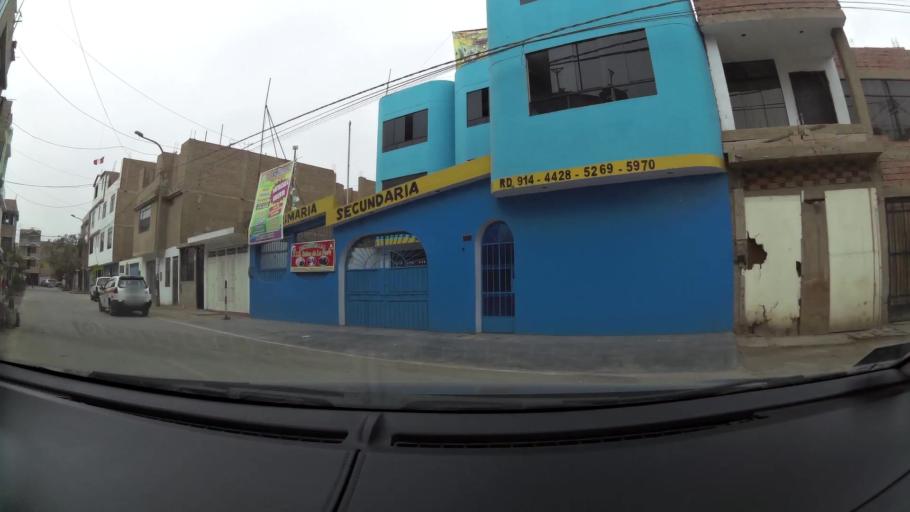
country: PE
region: Lima
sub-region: Lima
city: Independencia
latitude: -11.9686
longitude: -77.0906
